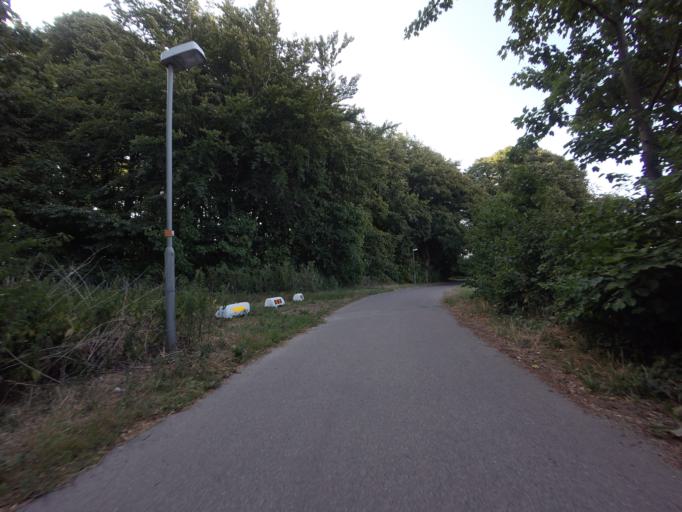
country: SE
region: Skane
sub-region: Landskrona
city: Asmundtorp
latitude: 55.8631
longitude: 12.8880
